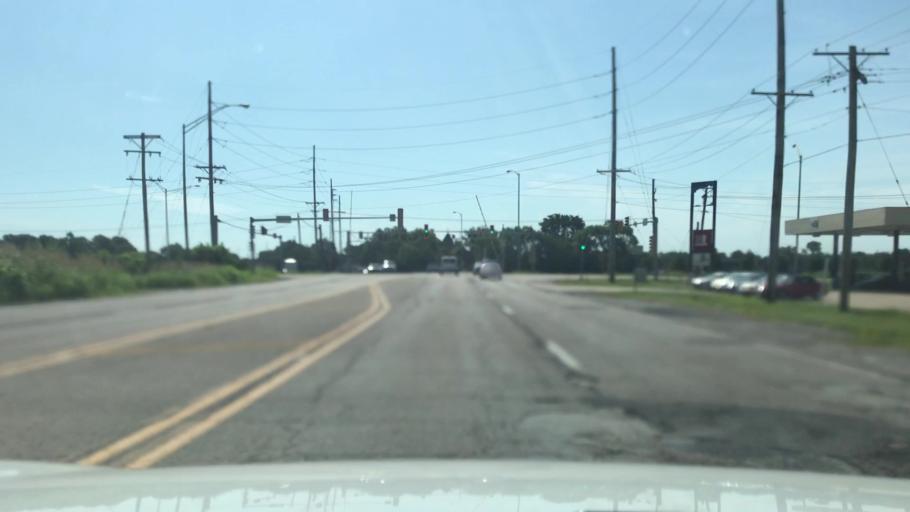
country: US
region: Illinois
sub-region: Madison County
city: Granite City
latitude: 38.7322
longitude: -90.1381
